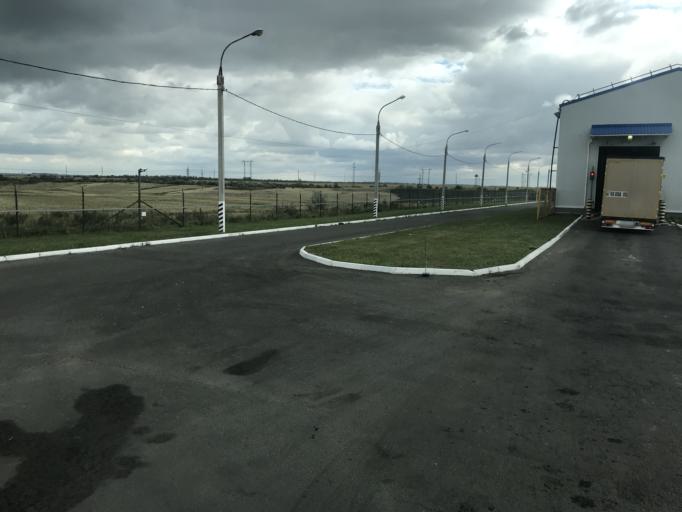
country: RU
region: Chelyabinsk
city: Troitsk
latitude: 54.0075
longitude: 61.6266
